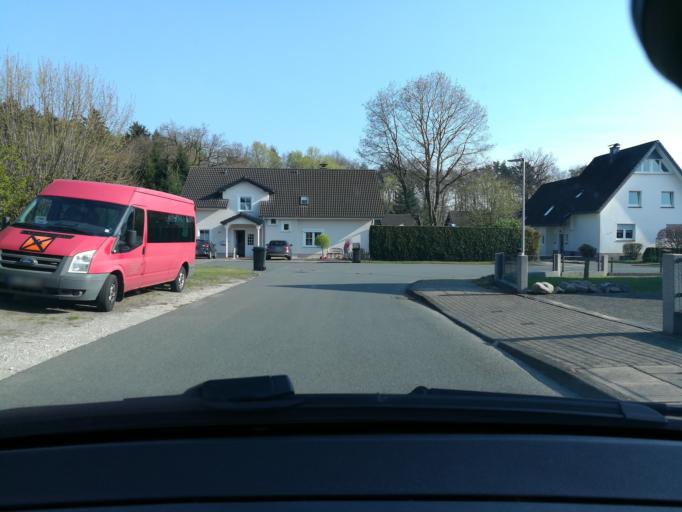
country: DE
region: North Rhine-Westphalia
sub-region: Regierungsbezirk Detmold
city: Oerlinghausen
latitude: 51.9284
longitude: 8.6055
